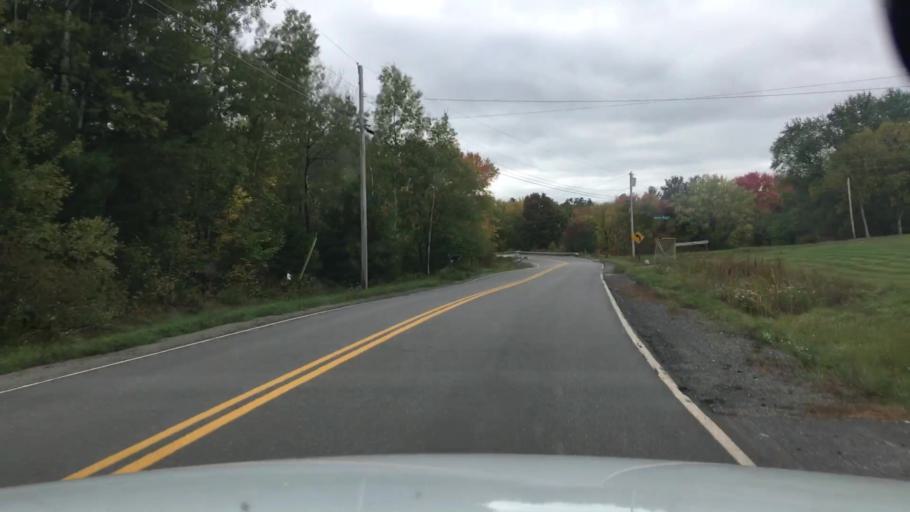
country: US
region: Maine
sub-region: Penobscot County
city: Hudson
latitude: 44.9869
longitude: -68.7732
